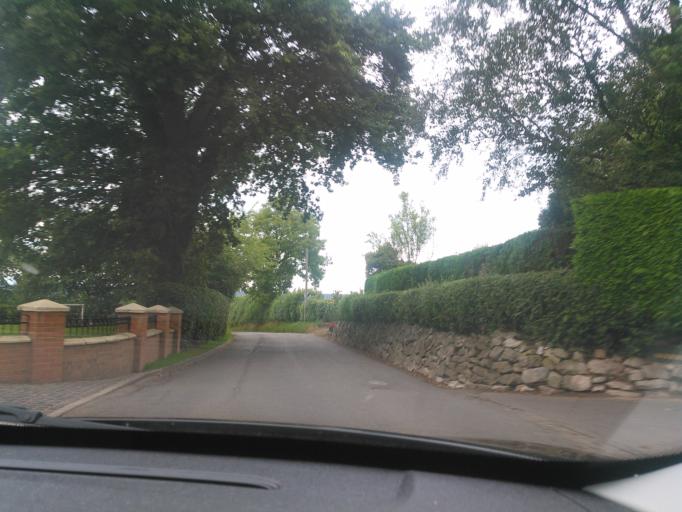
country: GB
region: England
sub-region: Shropshire
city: Prees
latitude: 52.8559
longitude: -2.6491
